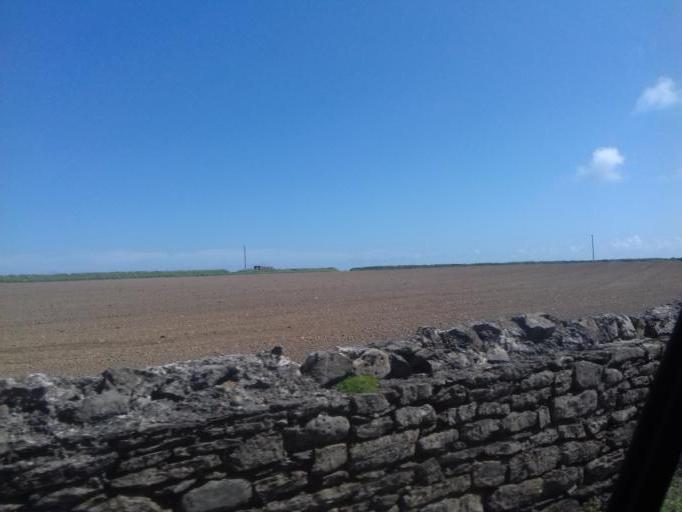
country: IE
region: Munster
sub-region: Waterford
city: Dunmore East
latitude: 52.1279
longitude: -6.9292
